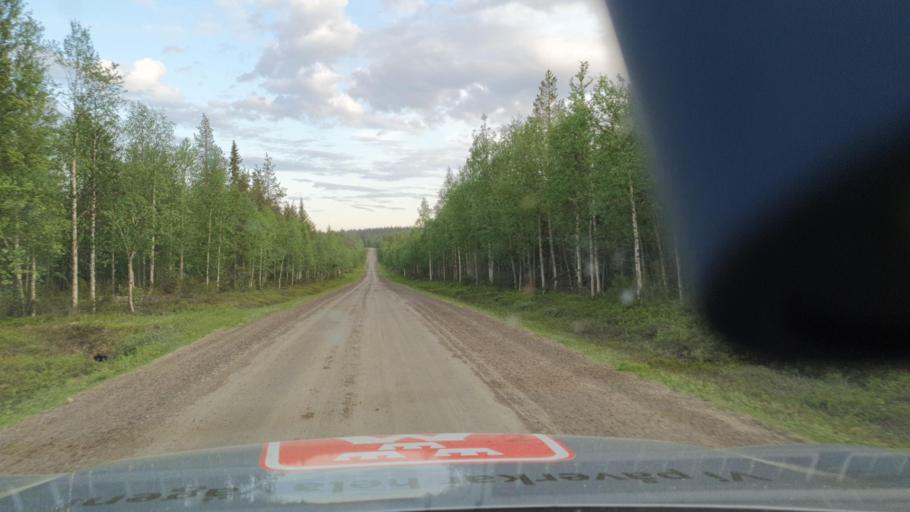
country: SE
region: Norrbotten
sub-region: Bodens Kommun
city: Boden
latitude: 66.5479
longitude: 21.4666
